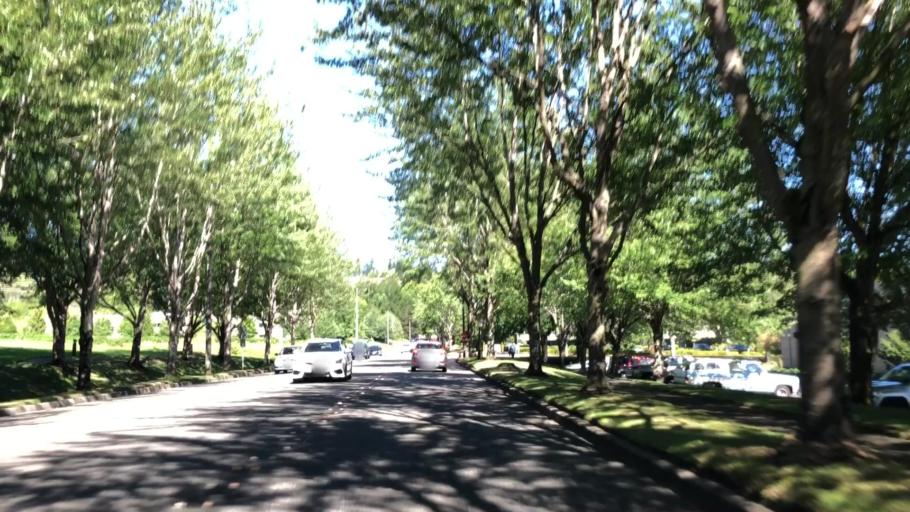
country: US
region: Washington
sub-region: Snohomish County
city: North Creek
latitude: 47.7993
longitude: -122.2033
